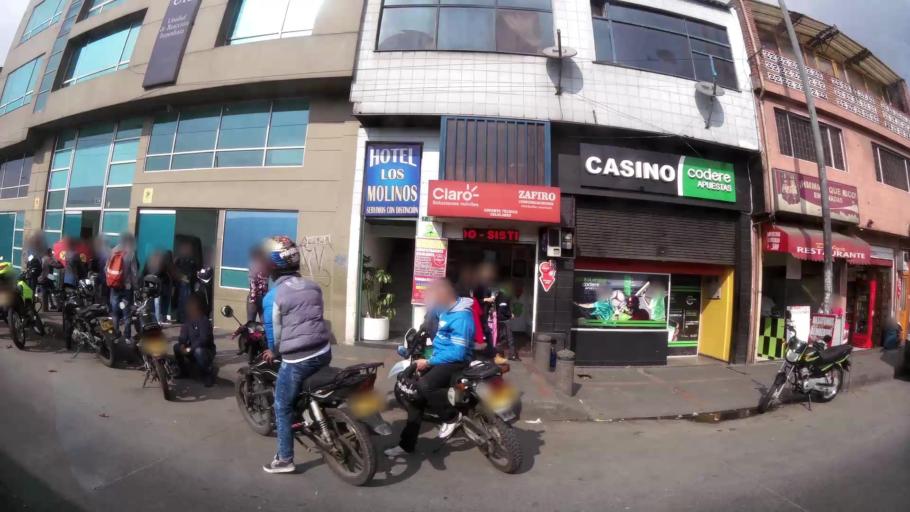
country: CO
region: Bogota D.C.
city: Bogota
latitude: 4.5573
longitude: -74.1218
